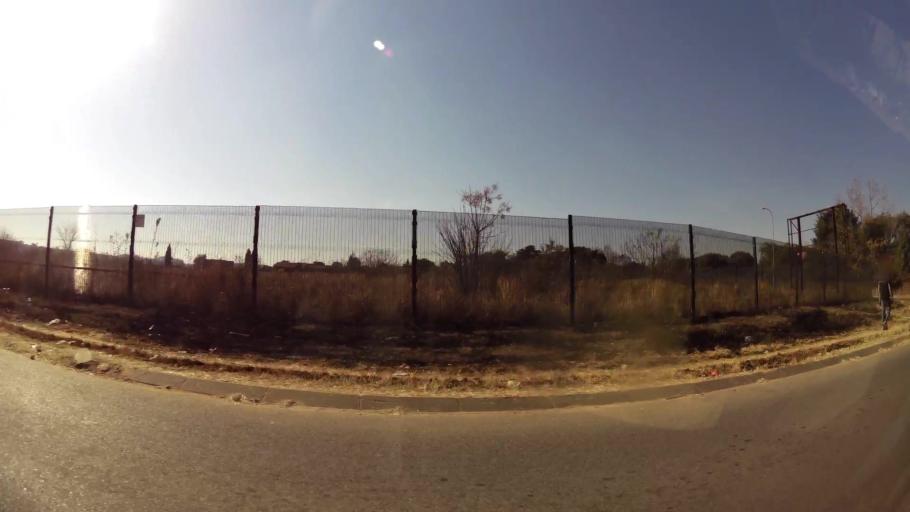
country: ZA
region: Gauteng
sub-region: City of Johannesburg Metropolitan Municipality
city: Modderfontein
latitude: -26.1124
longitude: 28.1150
